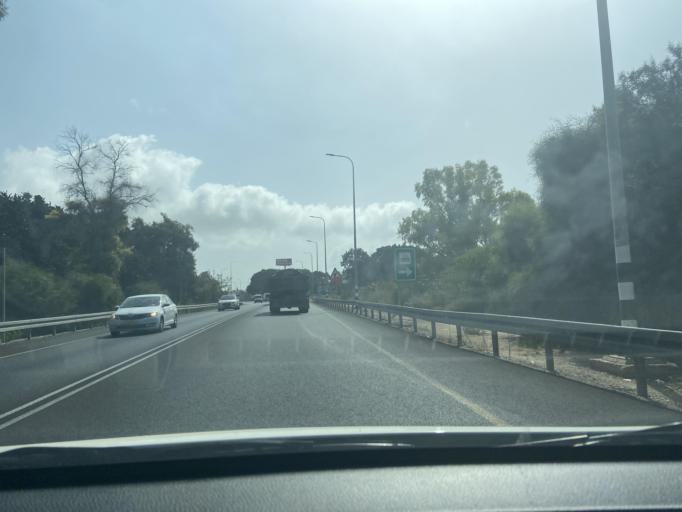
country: IL
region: Northern District
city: Nahariya
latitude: 33.0359
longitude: 35.1047
